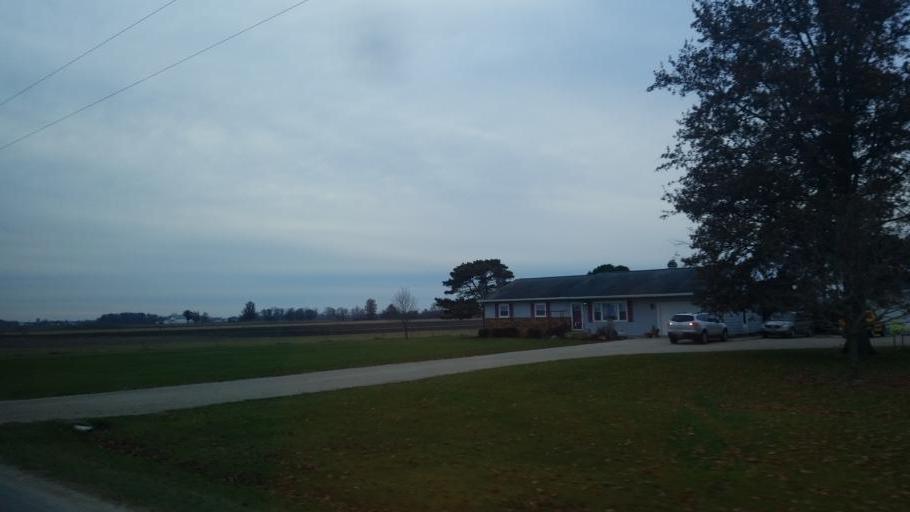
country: US
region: Indiana
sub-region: Adams County
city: Berne
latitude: 40.7135
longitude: -84.8793
